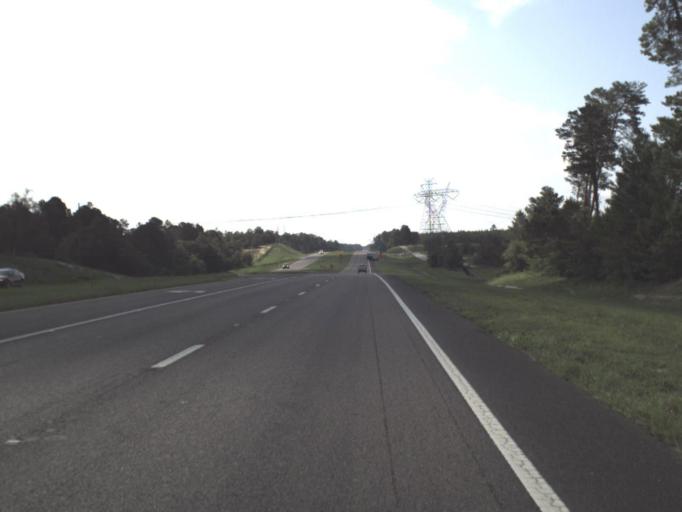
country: US
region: Florida
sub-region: Citrus County
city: Sugarmill Woods
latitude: 28.6927
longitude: -82.5050
